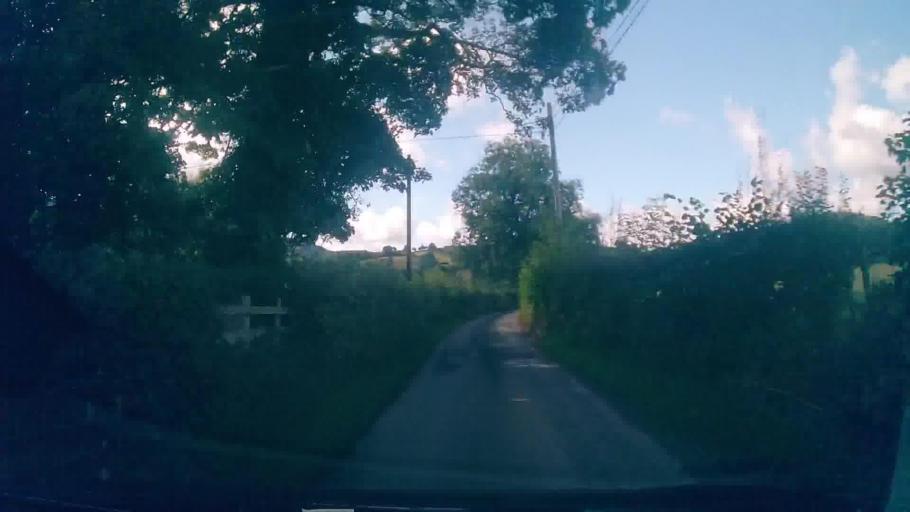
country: GB
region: Wales
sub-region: Sir Powys
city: Llangynog
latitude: 52.8059
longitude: -3.3664
